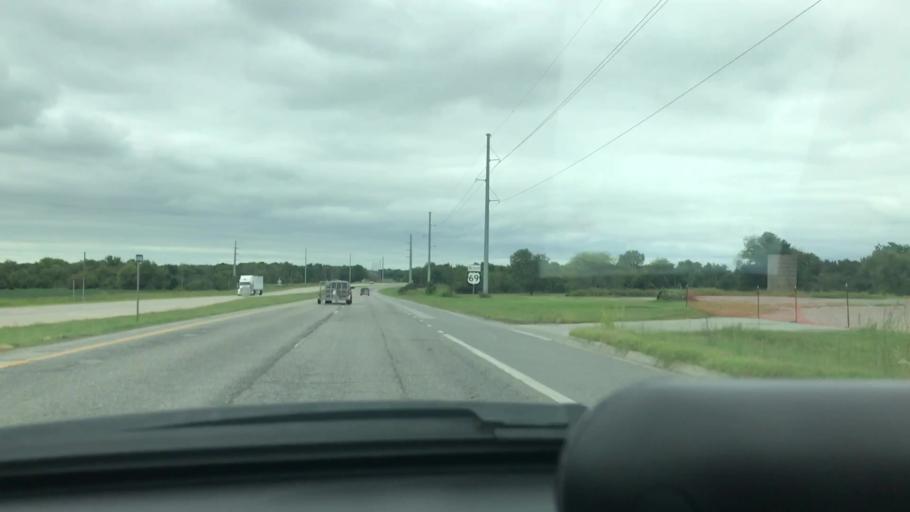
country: US
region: Oklahoma
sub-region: Wagoner County
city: Wagoner
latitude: 36.0174
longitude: -95.3686
